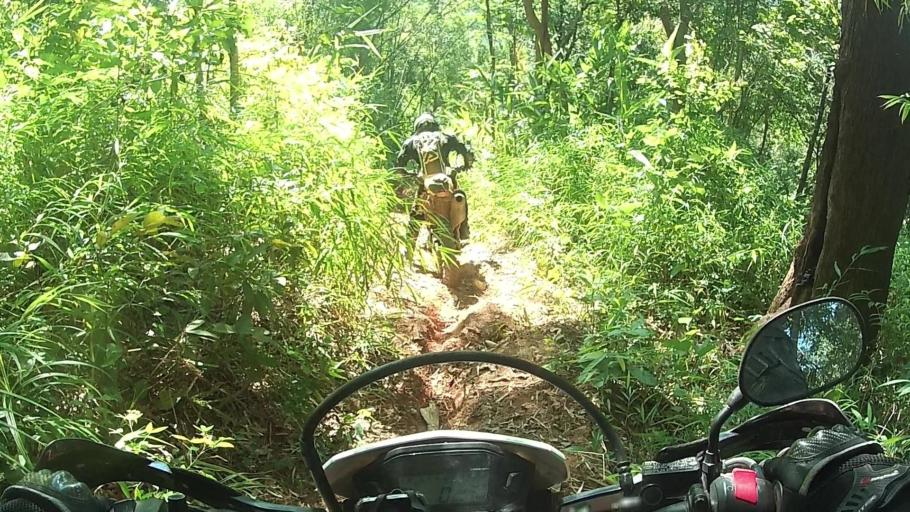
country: TH
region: Chiang Mai
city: Phrao
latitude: 19.3719
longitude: 99.3210
